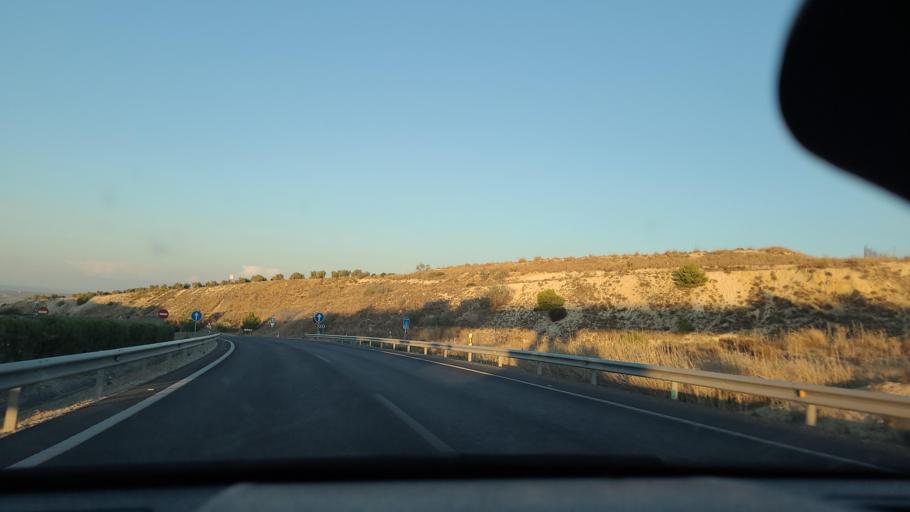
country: ES
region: Andalusia
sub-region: Provincia de Jaen
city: Jaen
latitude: 37.7876
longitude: -3.8292
